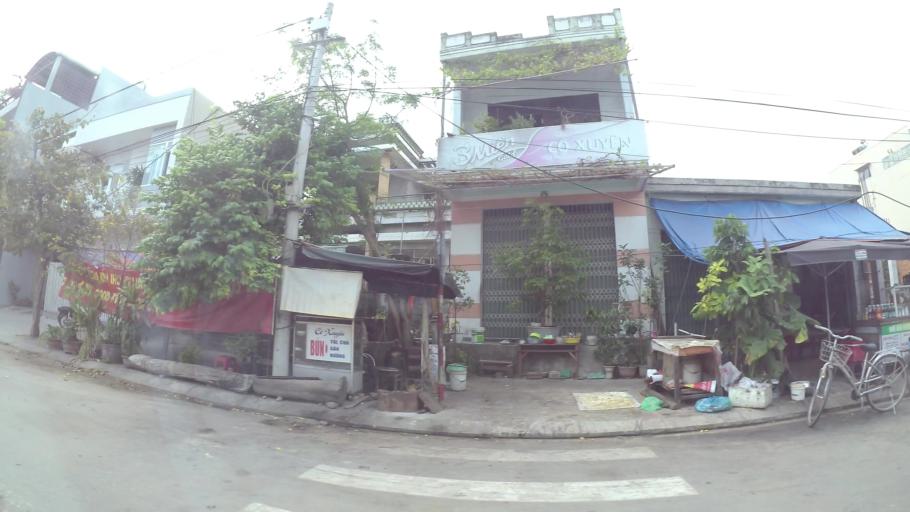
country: VN
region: Da Nang
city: Son Tra
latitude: 16.0874
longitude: 108.2435
